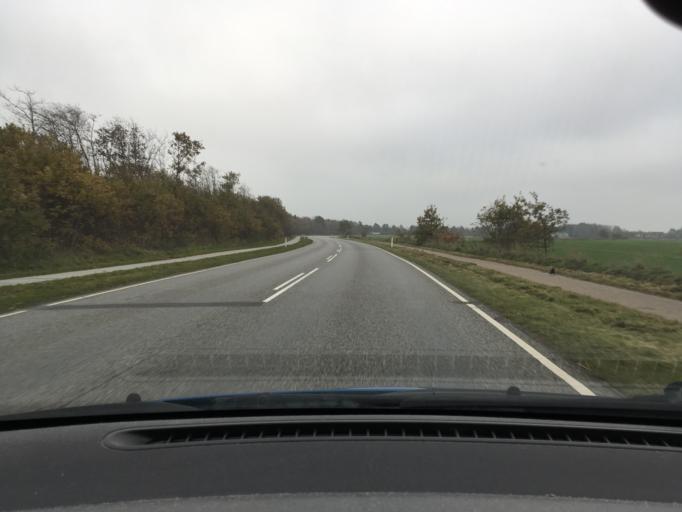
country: DK
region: South Denmark
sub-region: Tonder Kommune
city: Tonder
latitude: 54.9322
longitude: 8.8473
